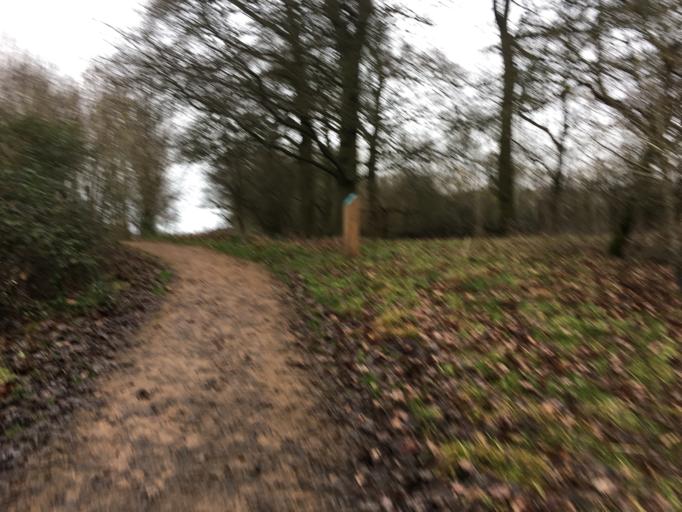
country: GB
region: England
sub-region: Warwickshire
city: Rugby
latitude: 52.3952
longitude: -1.2594
